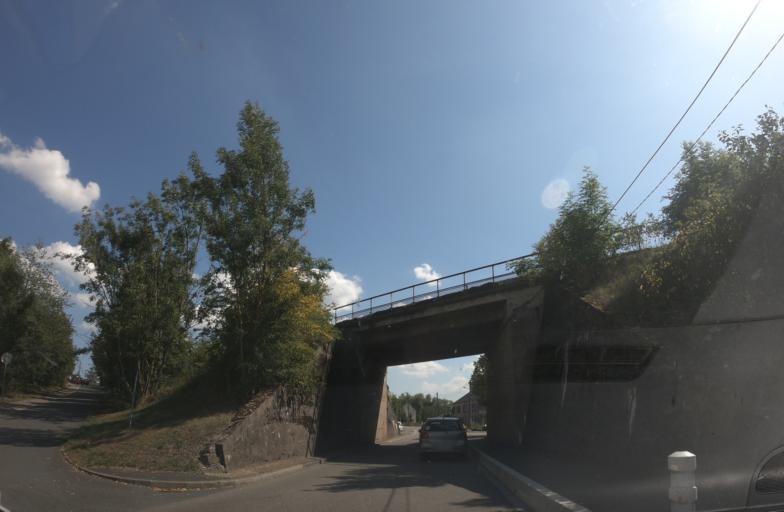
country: FR
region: Lorraine
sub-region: Departement de la Moselle
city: Diebling
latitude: 49.1052
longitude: 6.9588
